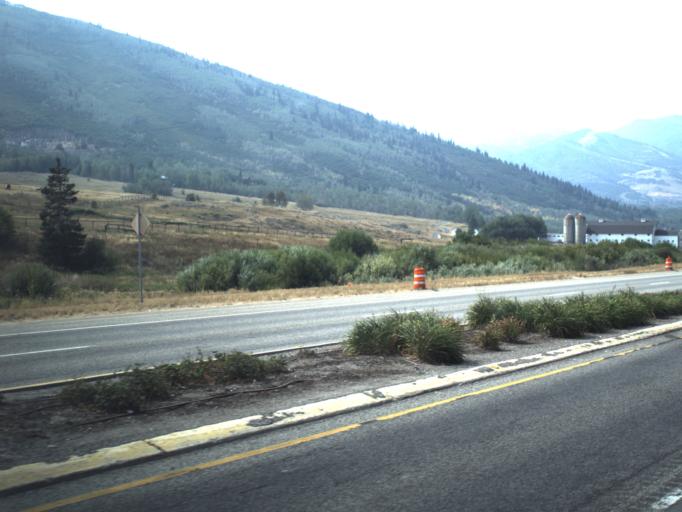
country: US
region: Utah
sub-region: Summit County
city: Snyderville
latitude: 40.6764
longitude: -111.5220
